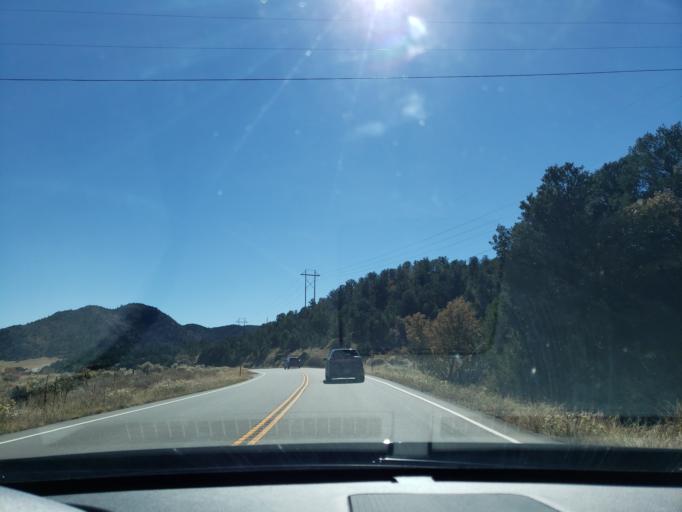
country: US
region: Colorado
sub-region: Fremont County
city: Canon City
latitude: 38.5912
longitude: -105.4243
